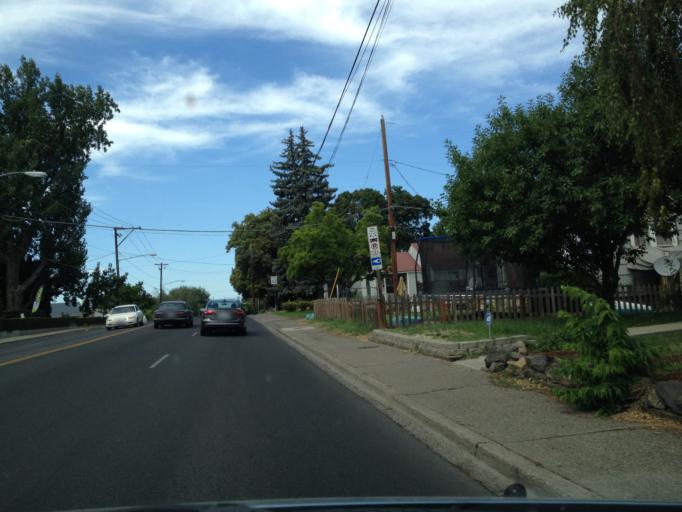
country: US
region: Washington
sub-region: Yakima County
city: Yakima
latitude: 46.5928
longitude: -120.5434
